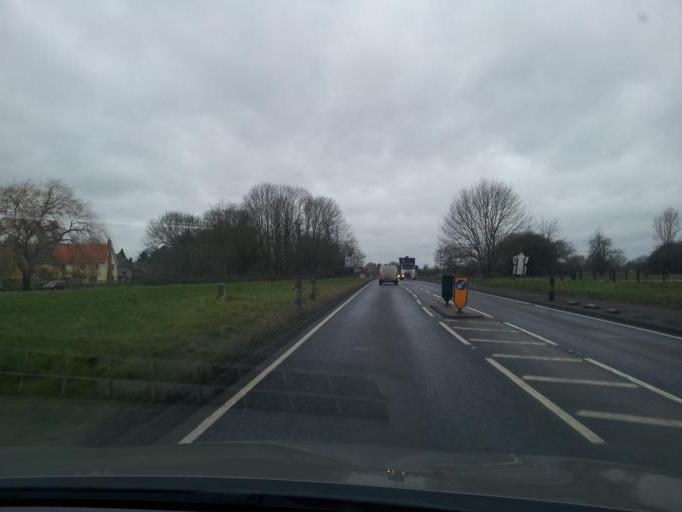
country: GB
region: England
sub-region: Norfolk
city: Diss
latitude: 52.3531
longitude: 1.0612
